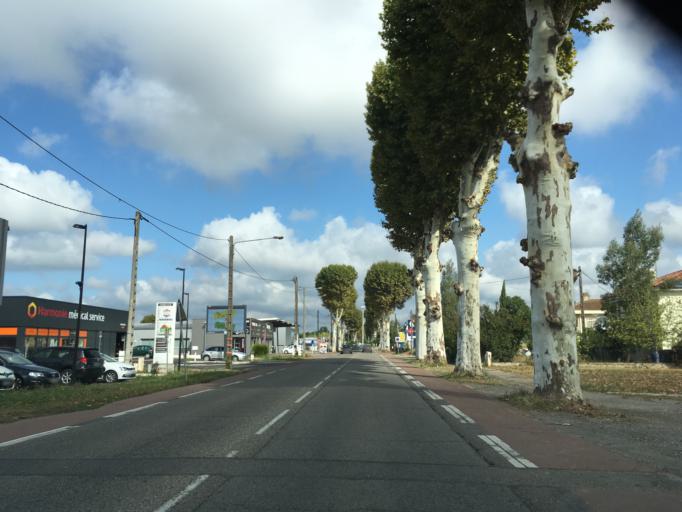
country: FR
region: Aquitaine
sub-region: Departement du Lot-et-Garonne
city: Agen
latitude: 44.1817
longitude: 0.6232
